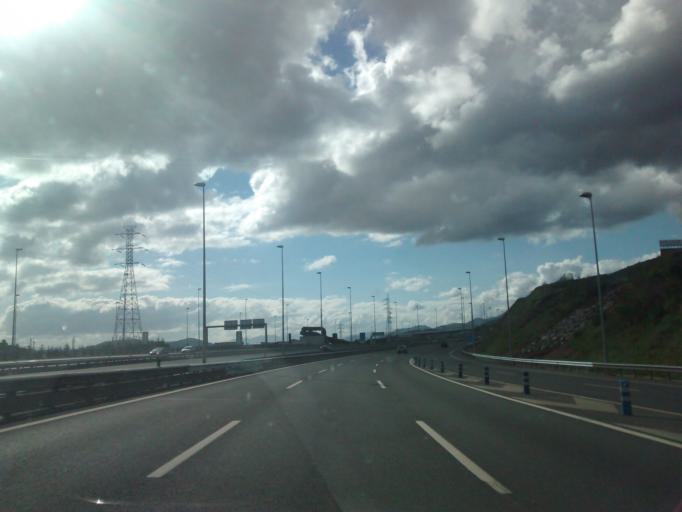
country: ES
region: Basque Country
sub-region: Bizkaia
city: Portugalete
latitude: 43.3107
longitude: -3.0314
